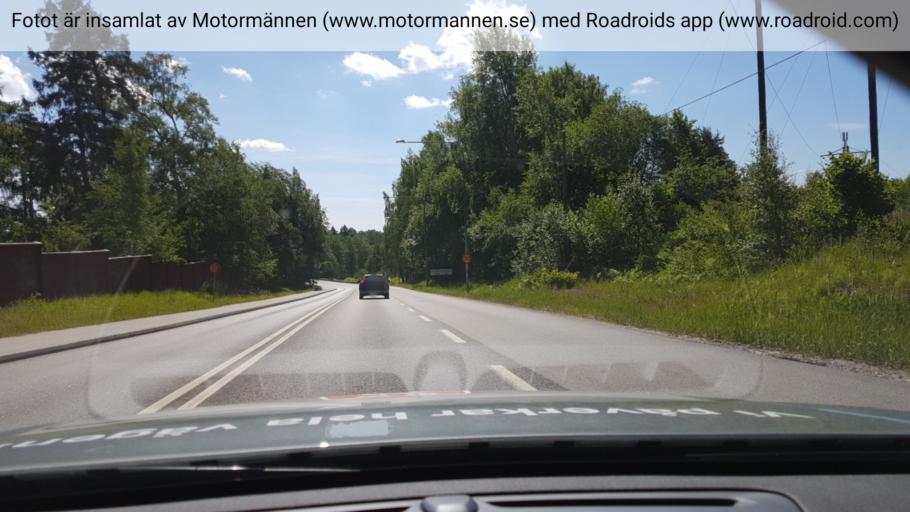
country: SE
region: Stockholm
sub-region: Tyreso Kommun
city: Bollmora
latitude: 59.2325
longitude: 18.1942
